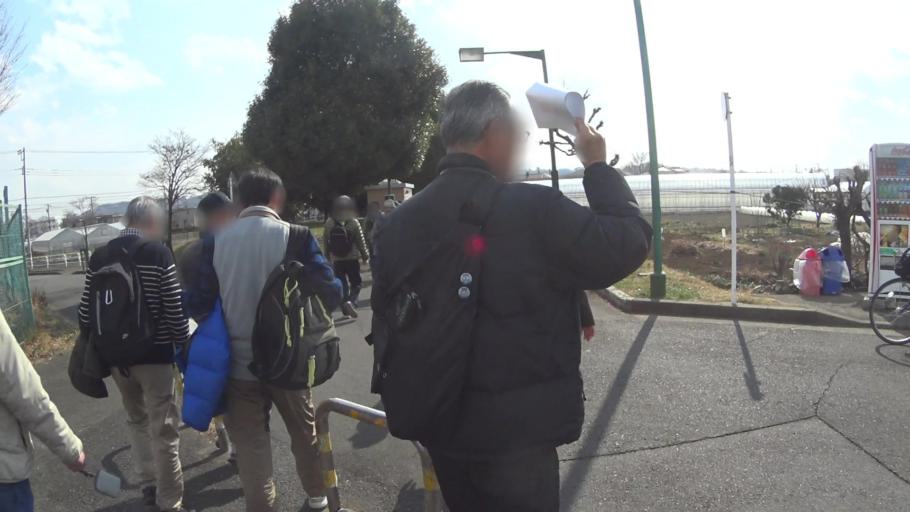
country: JP
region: Tokyo
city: Kokubunji
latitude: 35.6606
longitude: 139.4730
